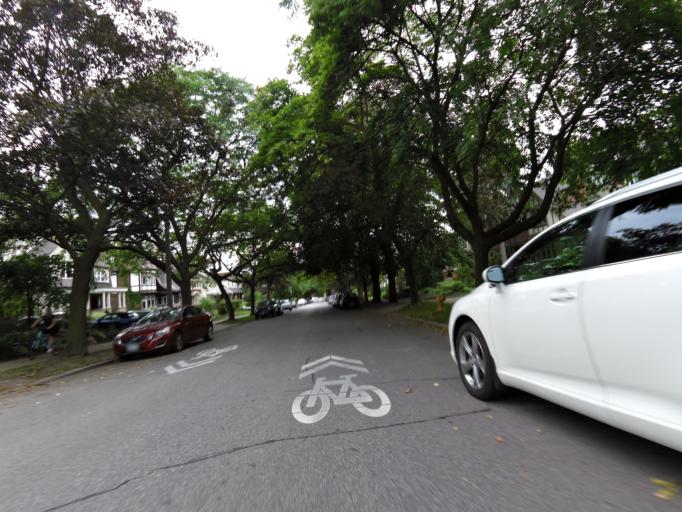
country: CA
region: Ontario
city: Toronto
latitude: 43.6455
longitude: -79.4536
